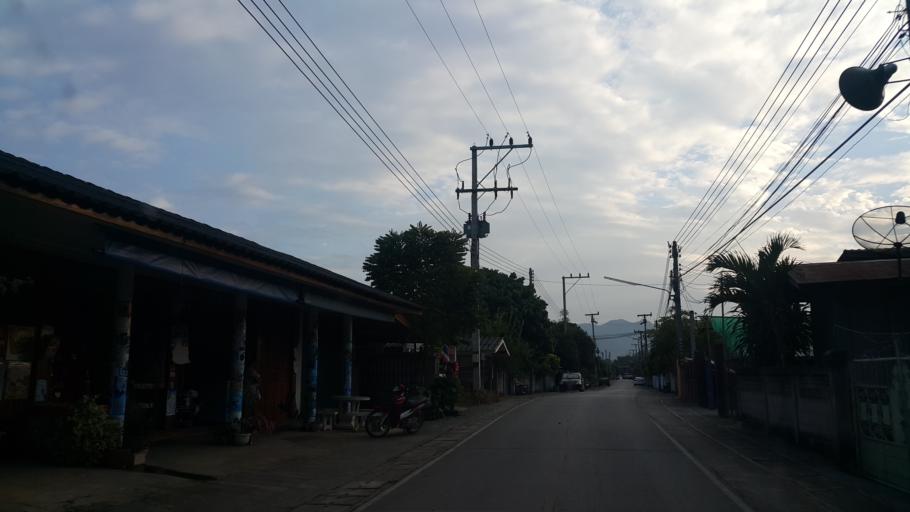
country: TH
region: Lampang
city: Sop Prap
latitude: 17.8667
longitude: 99.3305
